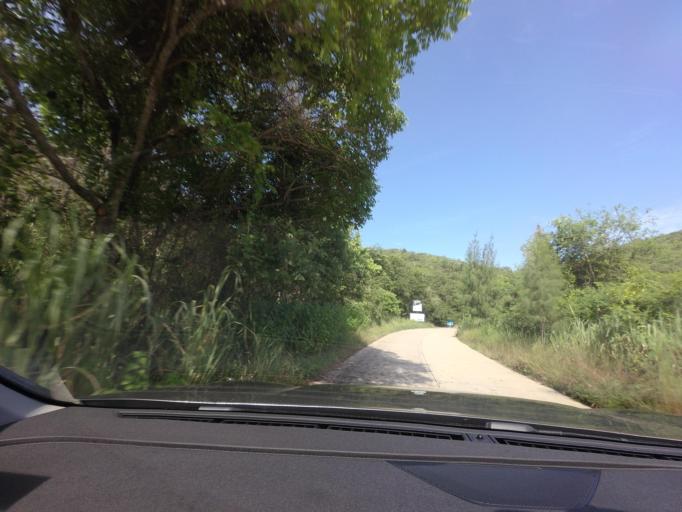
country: TH
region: Prachuap Khiri Khan
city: Hua Hin
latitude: 12.4846
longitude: 99.9428
